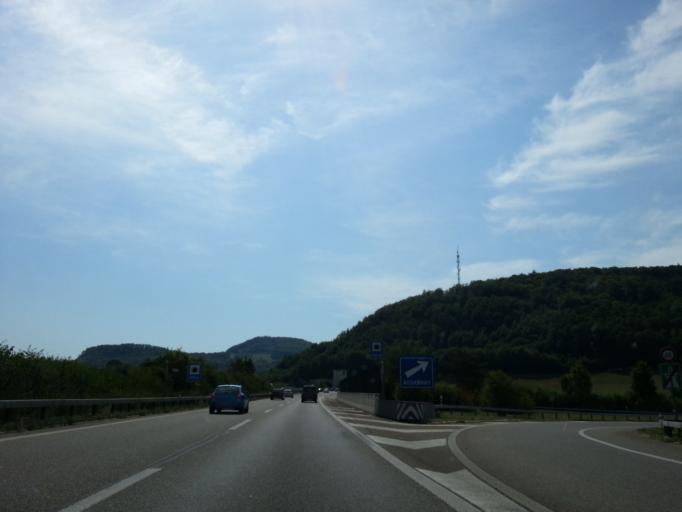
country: CH
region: Basel-Landschaft
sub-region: Bezirk Sissach
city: Sissach
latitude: 47.4673
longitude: 7.7975
